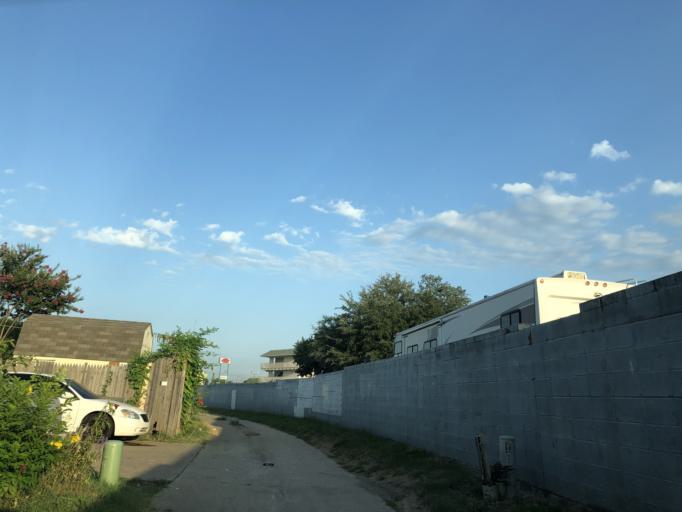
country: US
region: Texas
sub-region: Dallas County
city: Sunnyvale
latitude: 32.8400
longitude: -96.5911
